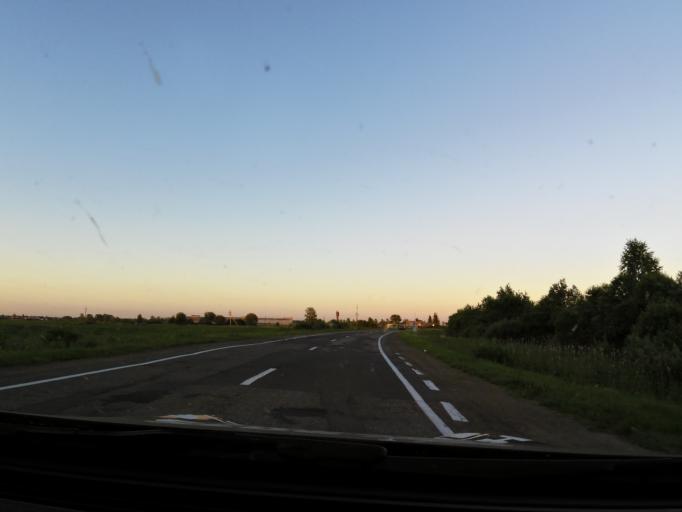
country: RU
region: Jaroslavl
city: Lyubim
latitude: 58.3570
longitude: 40.6479
